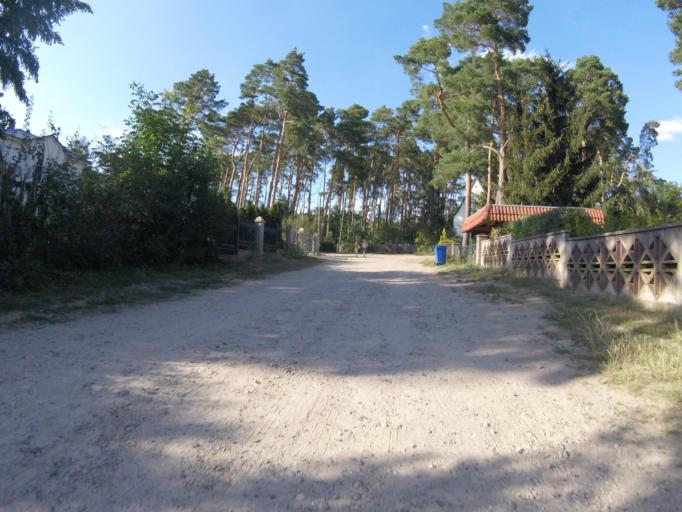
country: DE
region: Brandenburg
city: Wildau
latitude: 52.3128
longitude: 13.7044
